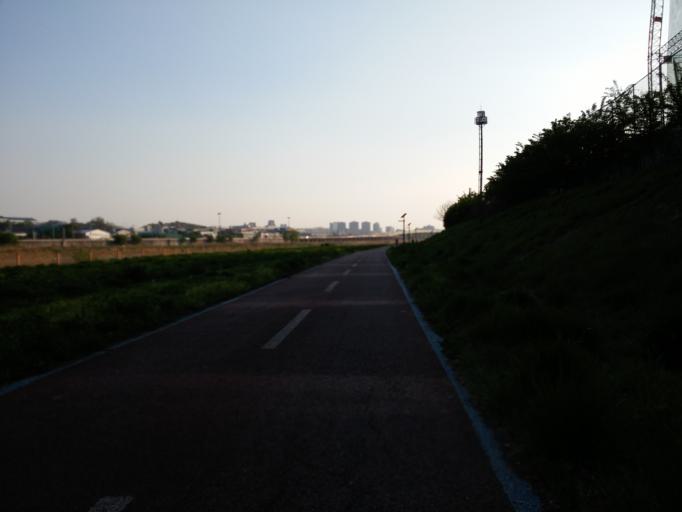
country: KR
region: Daejeon
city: Songgang-dong
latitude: 36.3785
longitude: 127.4080
